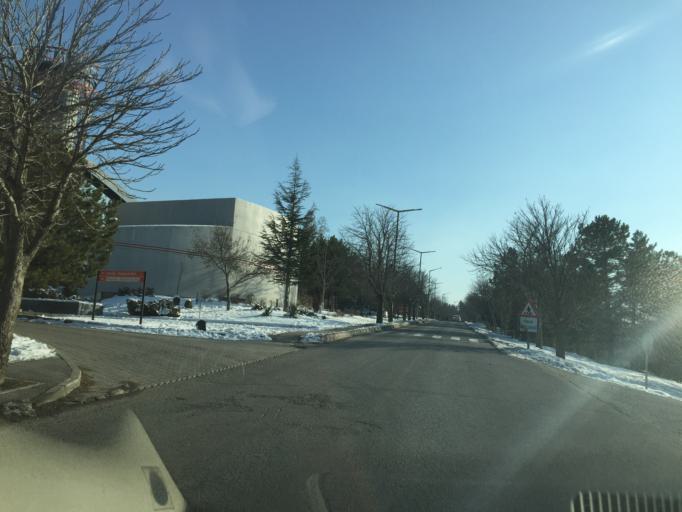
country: TR
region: Ankara
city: Ankara
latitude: 39.8912
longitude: 32.7812
